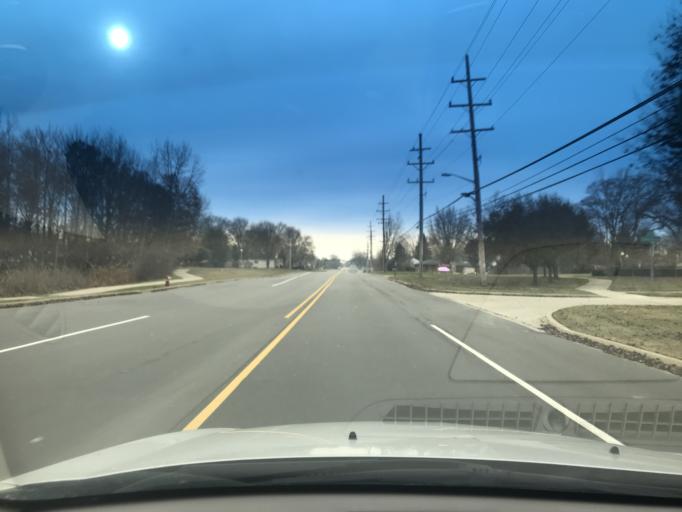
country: US
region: Michigan
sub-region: Macomb County
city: Shelby
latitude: 42.7017
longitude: -83.0546
